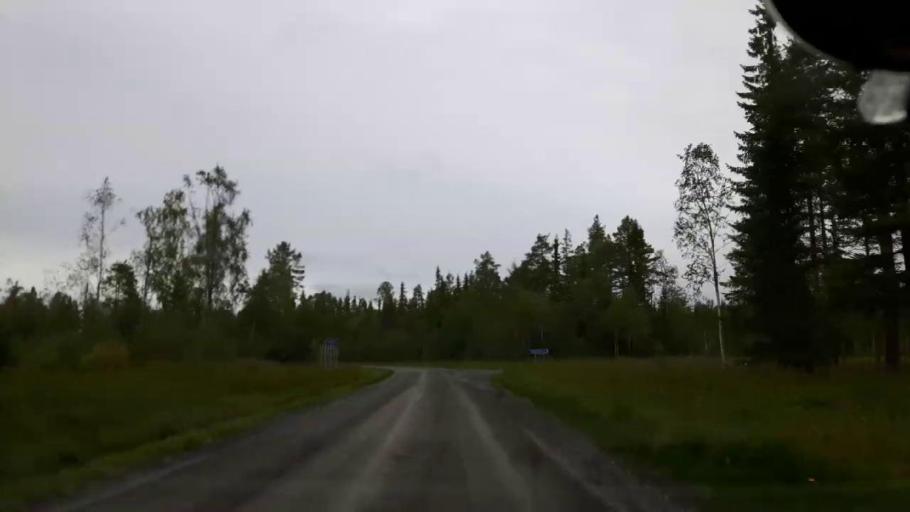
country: SE
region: Jaemtland
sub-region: Krokoms Kommun
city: Krokom
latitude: 63.2881
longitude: 14.3832
